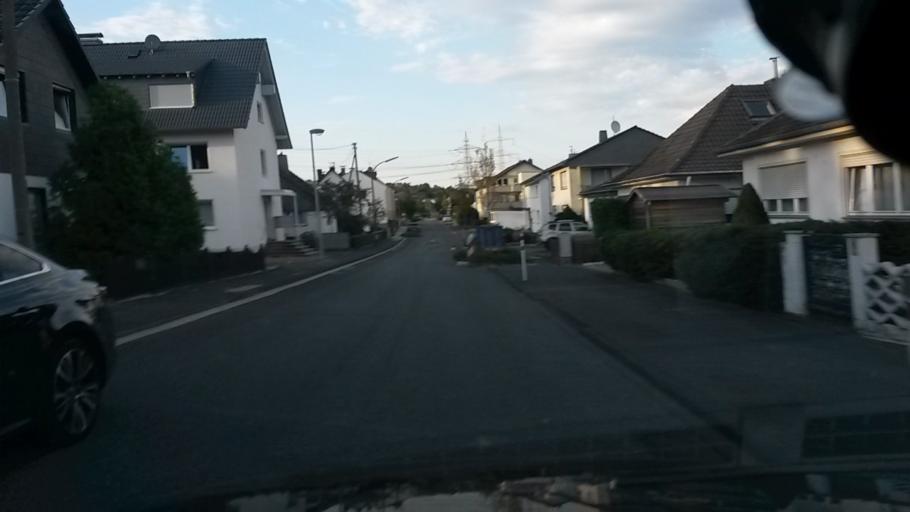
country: DE
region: North Rhine-Westphalia
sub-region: Regierungsbezirk Koln
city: Alfter
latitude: 50.7076
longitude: 7.0194
